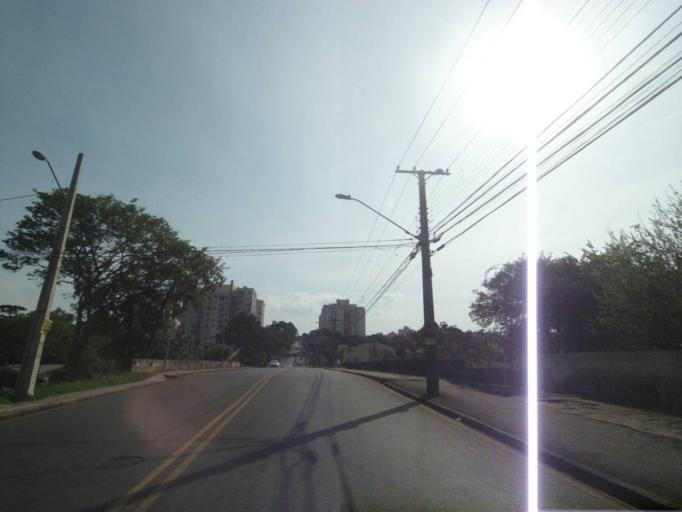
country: BR
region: Parana
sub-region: Curitiba
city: Curitiba
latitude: -25.4594
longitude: -49.3183
